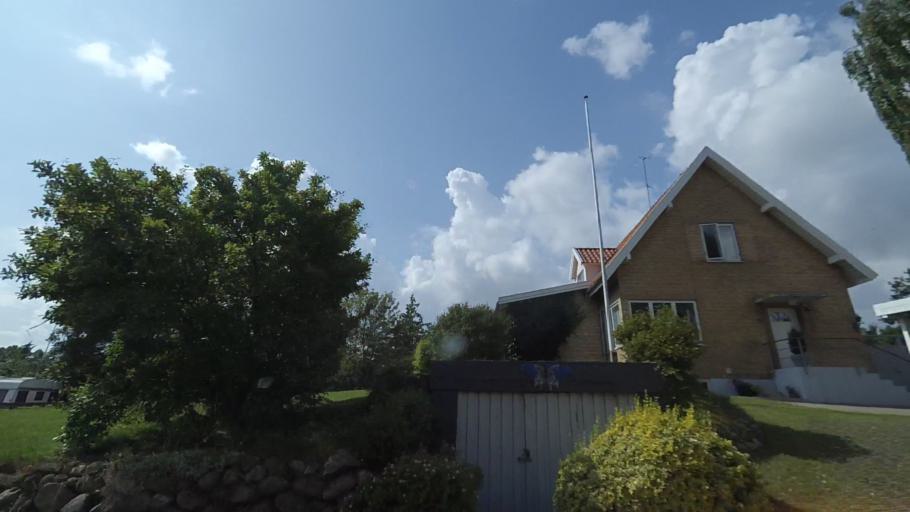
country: DK
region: Central Jutland
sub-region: Norddjurs Kommune
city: Allingabro
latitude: 56.5037
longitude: 10.3331
